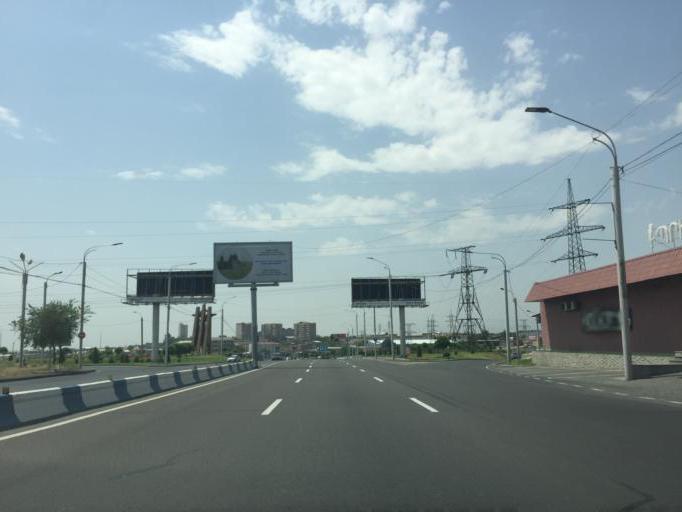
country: AM
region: Ararat
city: Argavand
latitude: 40.1588
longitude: 44.4466
